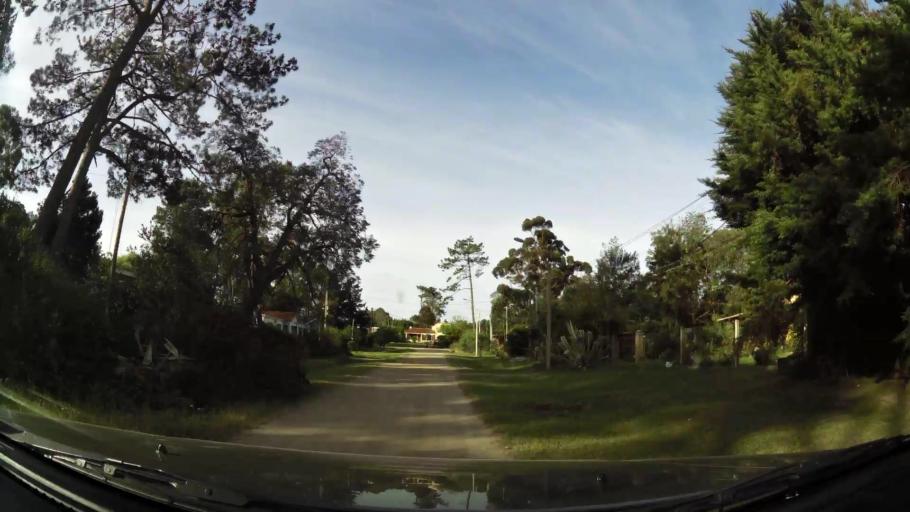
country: UY
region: Canelones
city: Empalme Olmos
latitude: -34.7873
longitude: -55.8579
